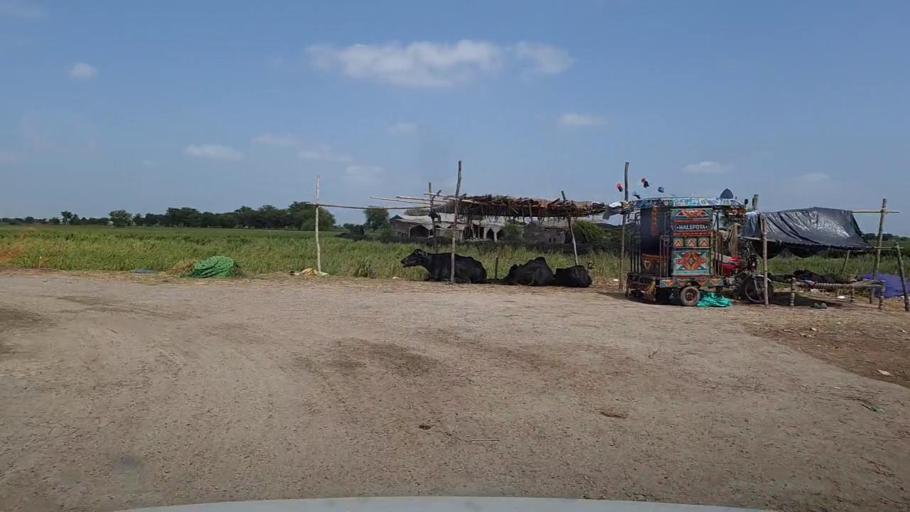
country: PK
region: Sindh
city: Kario
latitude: 24.6814
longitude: 68.5893
